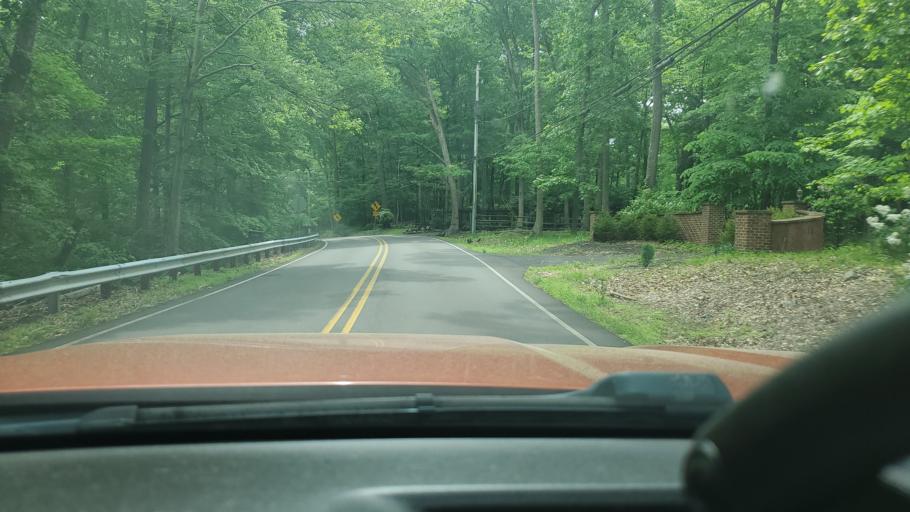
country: US
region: Pennsylvania
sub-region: Montgomery County
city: Red Hill
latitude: 40.3411
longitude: -75.4902
